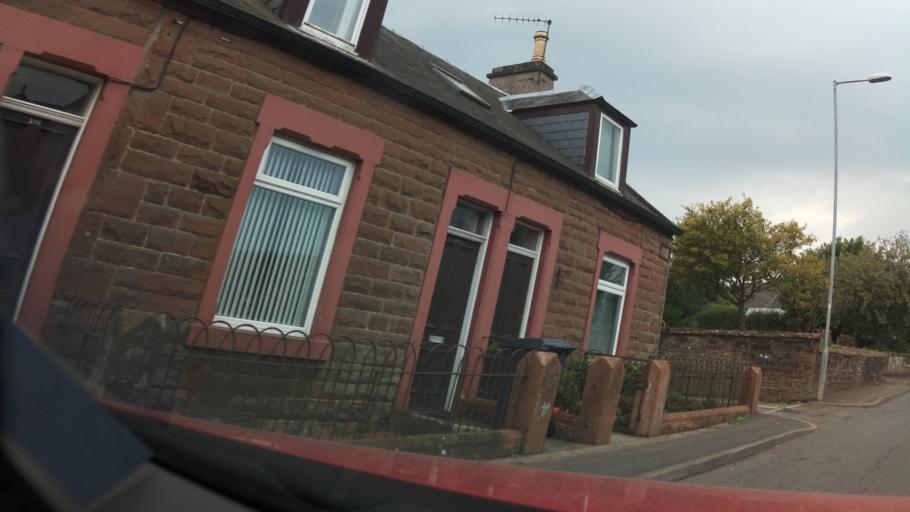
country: GB
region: Scotland
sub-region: Dumfries and Galloway
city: Locharbriggs
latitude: 55.0689
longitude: -3.5738
